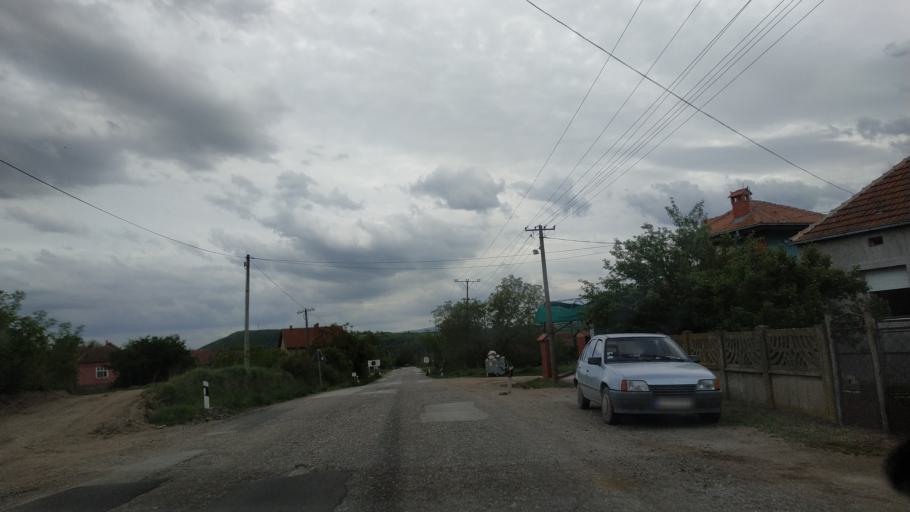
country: RS
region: Central Serbia
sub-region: Nisavski Okrug
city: Aleksinac
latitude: 43.6041
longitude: 21.6871
